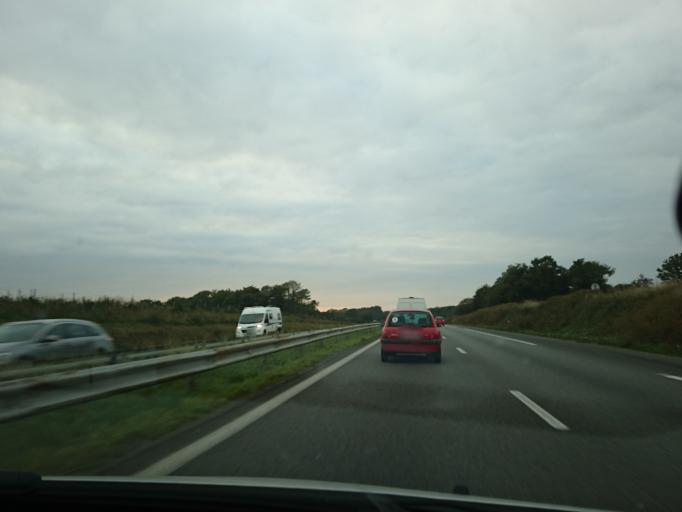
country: FR
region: Brittany
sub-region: Departement du Morbihan
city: Ploeren
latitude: 47.6613
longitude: -2.8353
